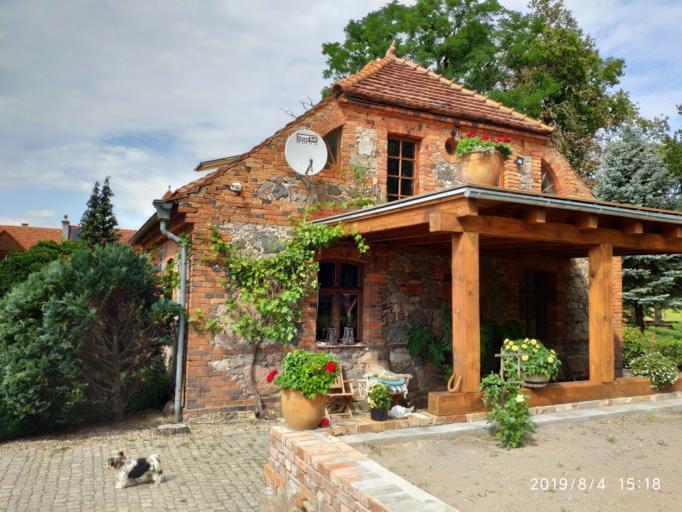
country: PL
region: Lubusz
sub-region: Powiat zielonogorski
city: Ochla
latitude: 51.8114
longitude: 15.4915
